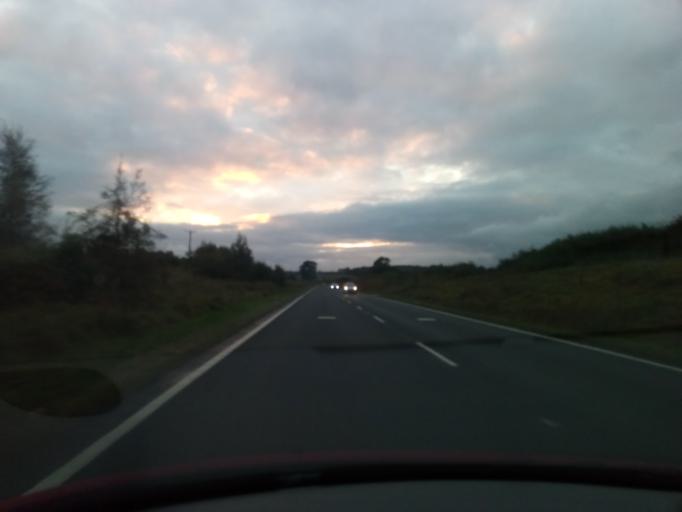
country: GB
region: England
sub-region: County Durham
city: High Etherley
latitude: 54.6257
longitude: -1.7177
